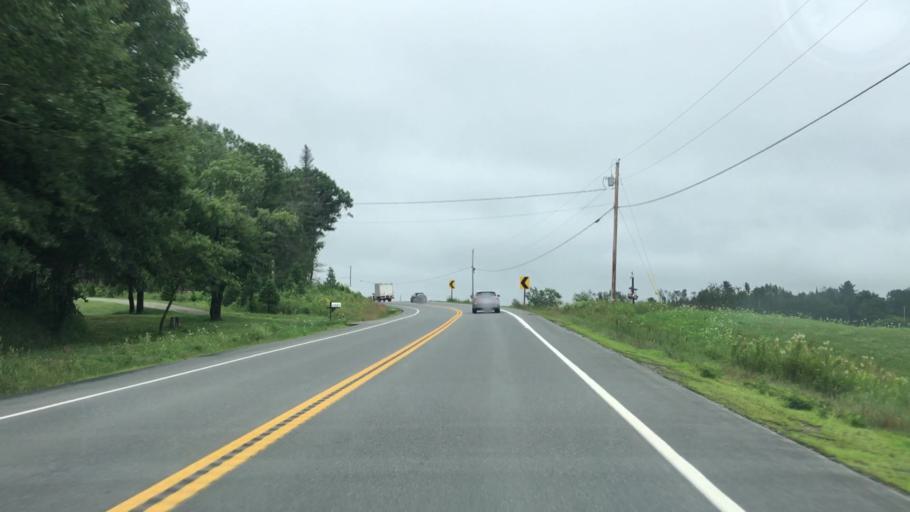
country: US
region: Maine
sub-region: Lincoln County
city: Jefferson
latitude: 44.2512
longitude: -69.4276
